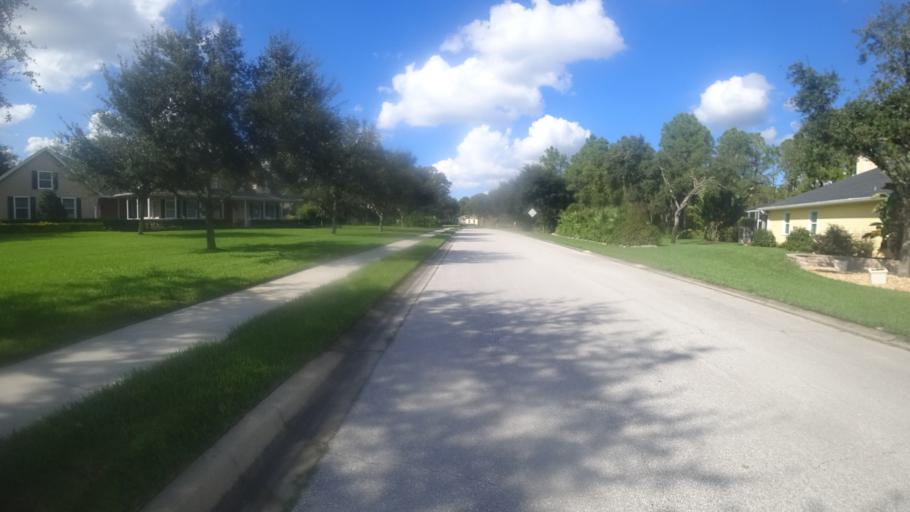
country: US
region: Florida
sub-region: Manatee County
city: Ellenton
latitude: 27.5445
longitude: -82.3804
